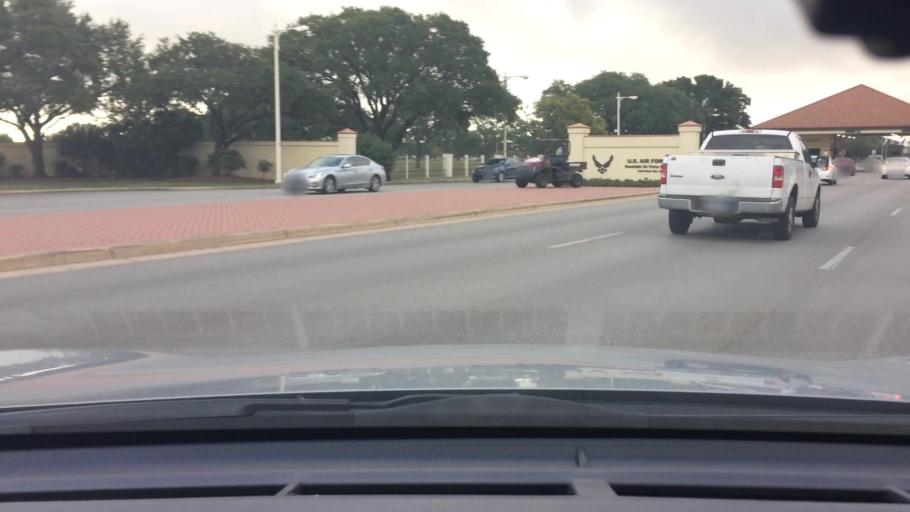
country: US
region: Texas
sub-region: Bexar County
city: Universal City
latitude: 29.5433
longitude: -98.2877
